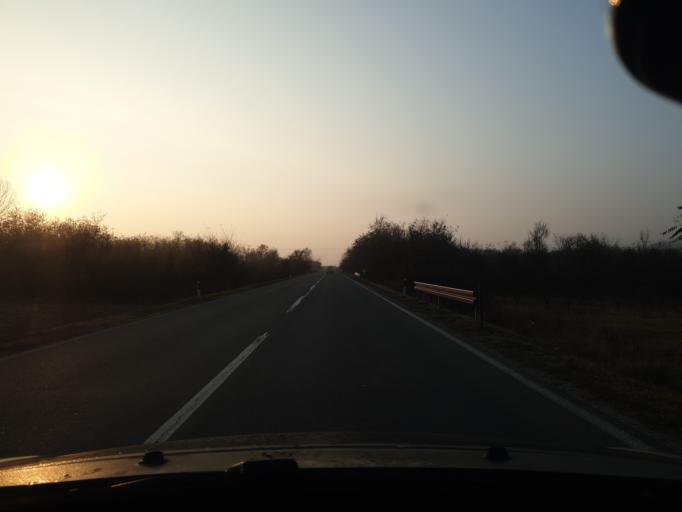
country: RS
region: Central Serbia
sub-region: Jablanicki Okrug
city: Leskovac
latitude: 42.9582
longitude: 21.9852
